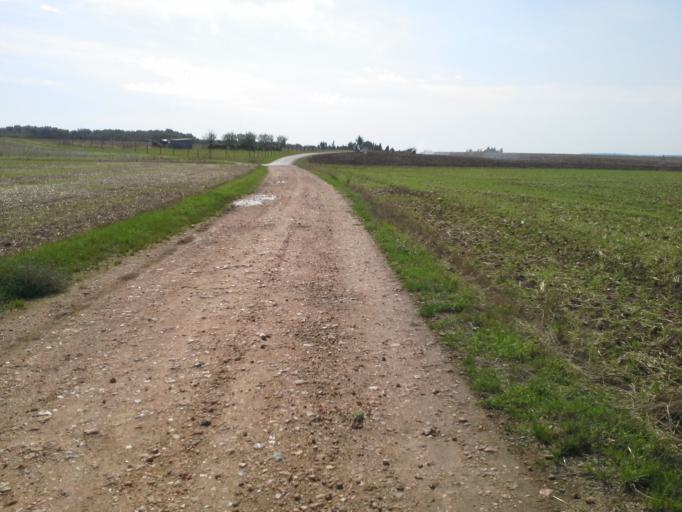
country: FR
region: Centre
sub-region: Departement du Loir-et-Cher
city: Villiers-sur-Loir
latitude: 47.8179
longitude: 0.9907
